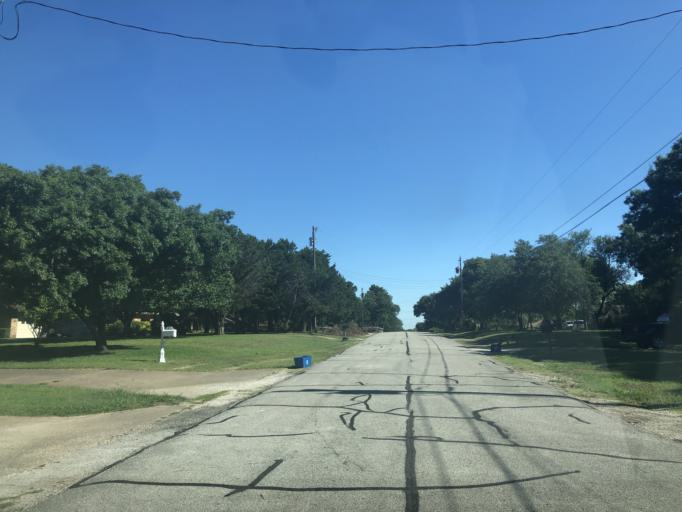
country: US
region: Texas
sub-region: Dallas County
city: Duncanville
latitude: 32.6582
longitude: -96.9391
